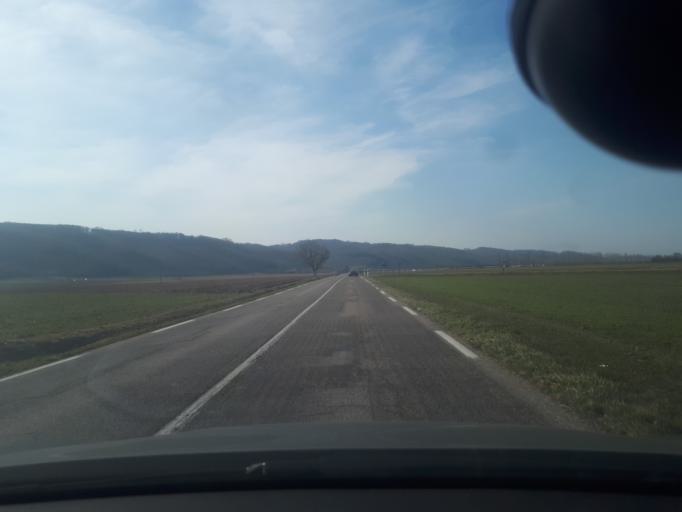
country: FR
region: Rhone-Alpes
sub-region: Departement de l'Isere
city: La Cote-Saint-Andre
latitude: 45.4263
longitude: 5.2732
